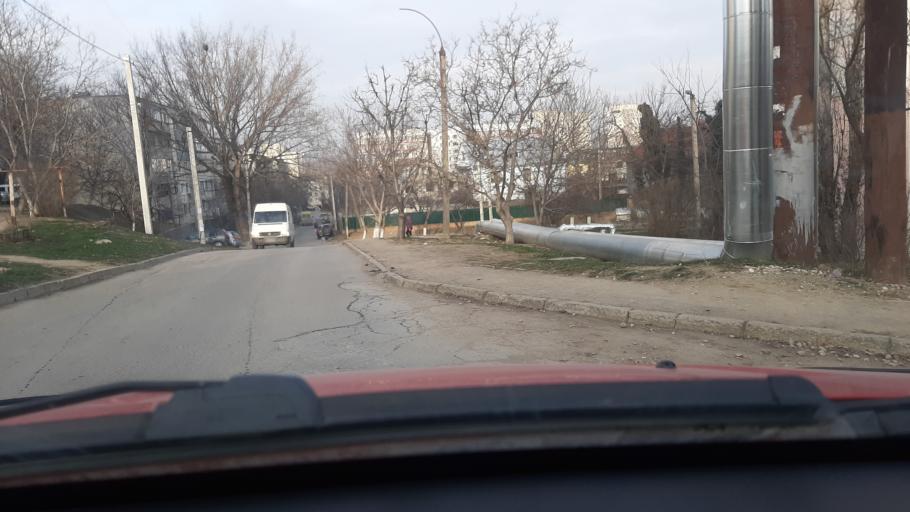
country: MD
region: Chisinau
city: Vatra
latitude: 47.0402
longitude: 28.7898
